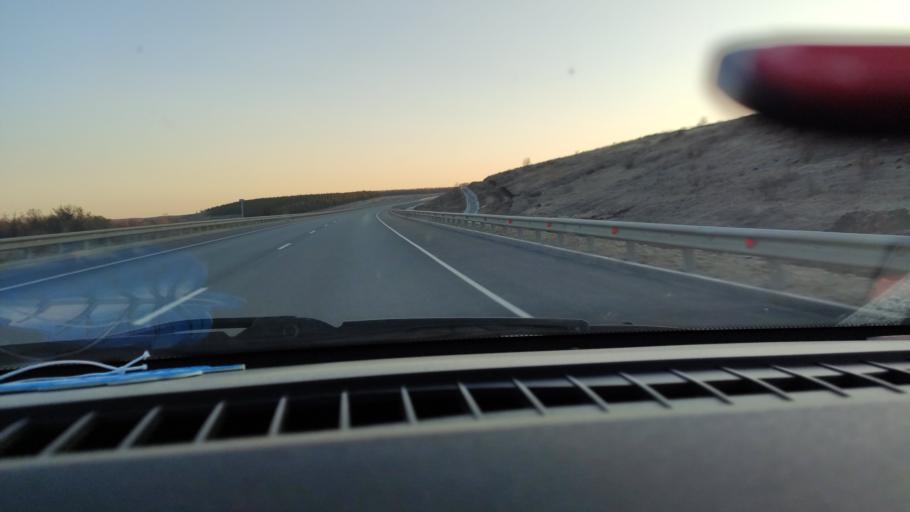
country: RU
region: Saratov
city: Yelshanka
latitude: 51.8724
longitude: 46.5042
